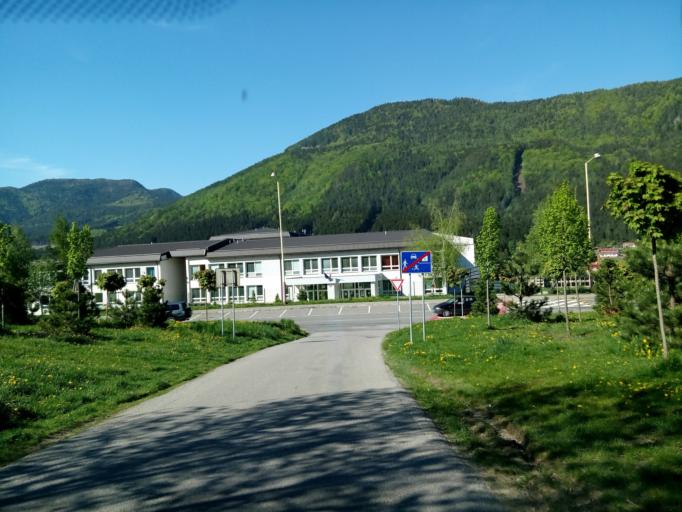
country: SK
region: Zilinsky
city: Ruzomberok
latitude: 49.0846
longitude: 19.2683
